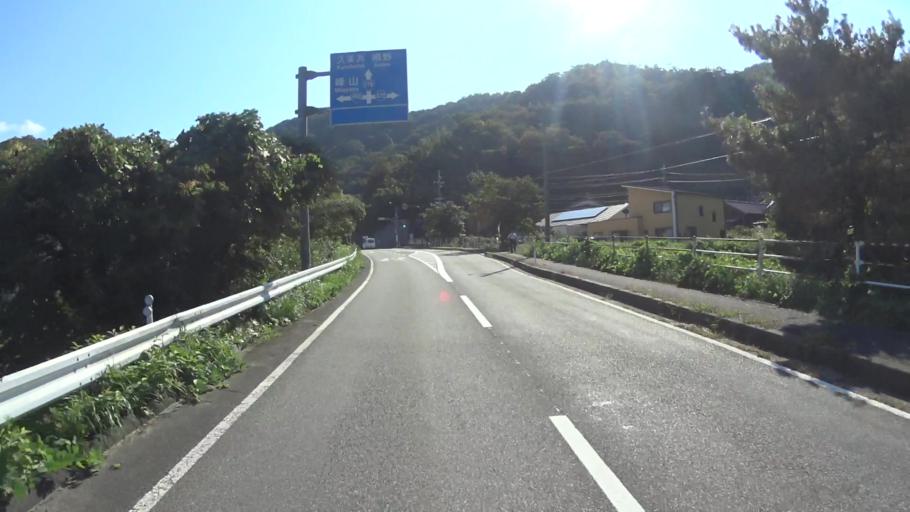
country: JP
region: Kyoto
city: Miyazu
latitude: 35.7321
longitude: 135.0966
